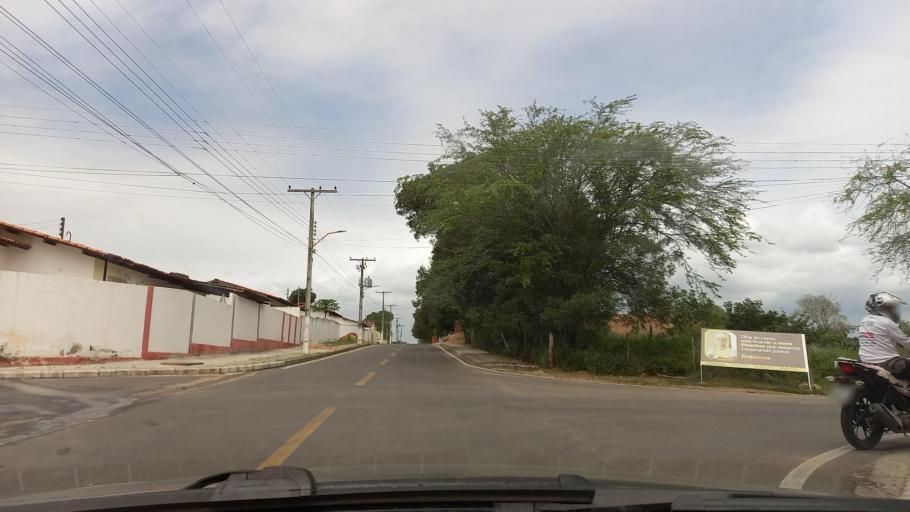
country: BR
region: Sergipe
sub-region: Caninde De Sao Francisco
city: Caninde de Sao Francisco
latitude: -9.6145
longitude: -37.7671
